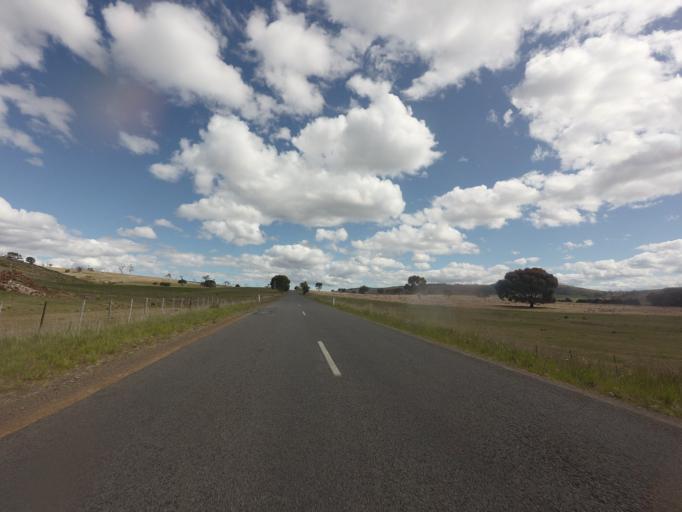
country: AU
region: Tasmania
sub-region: Brighton
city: Bridgewater
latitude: -42.3883
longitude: 147.3149
